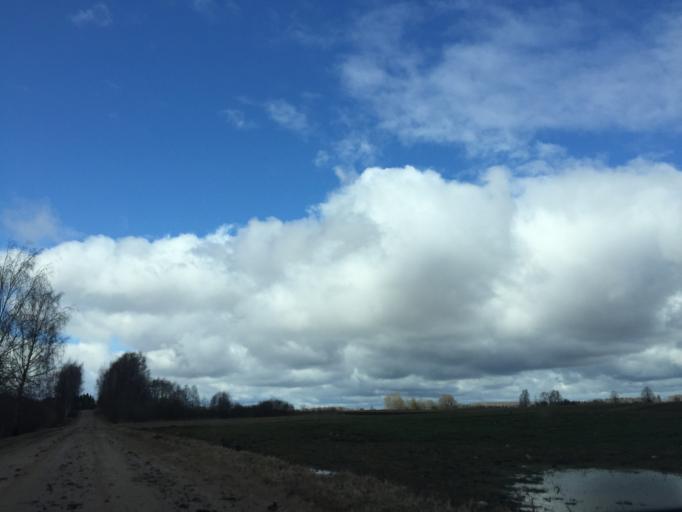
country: LV
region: Akniste
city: Akniste
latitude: 56.0935
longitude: 25.9917
